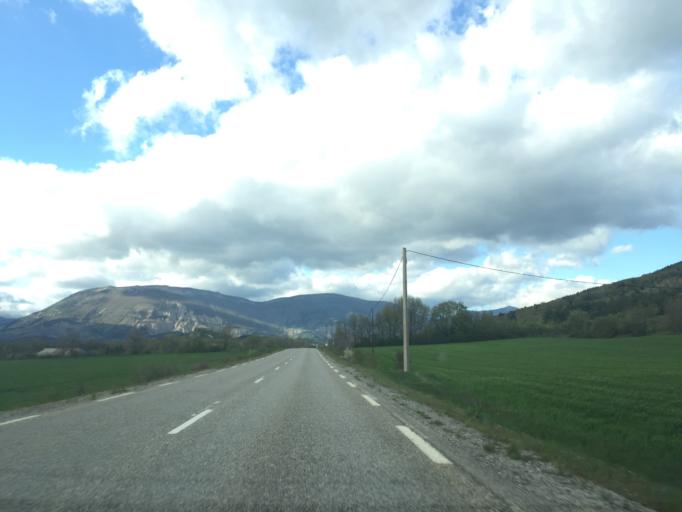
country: FR
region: Provence-Alpes-Cote d'Azur
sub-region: Departement des Hautes-Alpes
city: Serres
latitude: 44.4732
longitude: 5.7261
